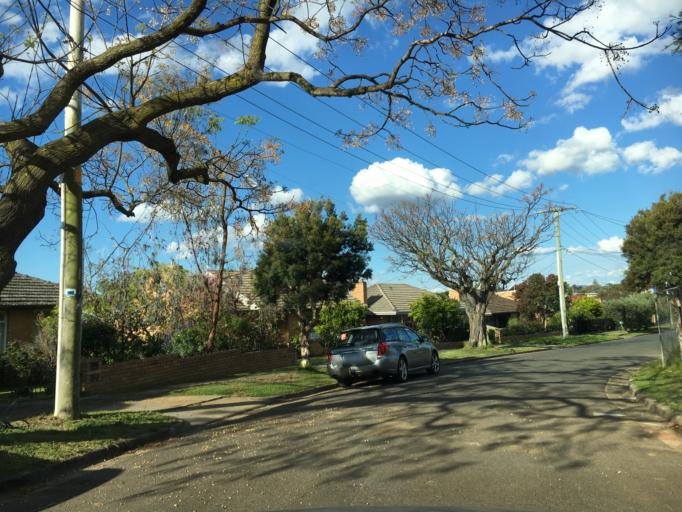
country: AU
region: Victoria
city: Clayton
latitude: -37.9005
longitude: 145.1114
